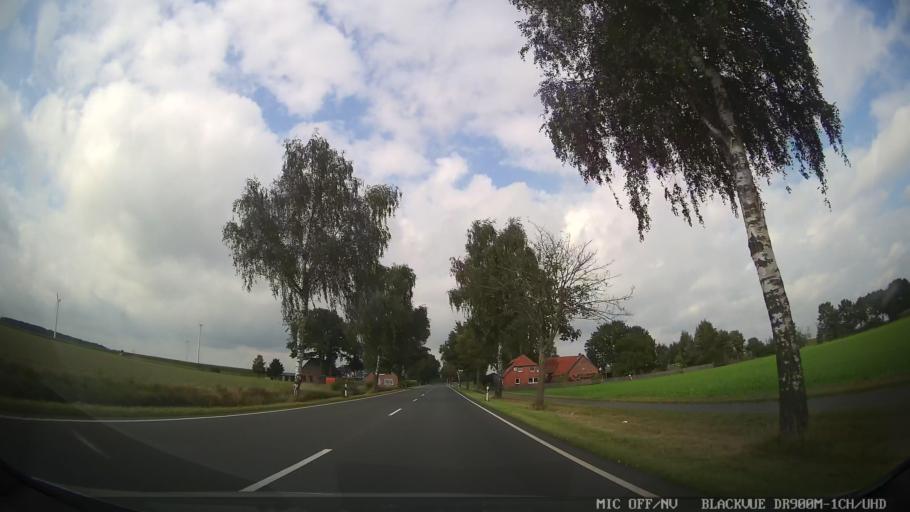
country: DE
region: Lower Saxony
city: Bergen
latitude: 52.7769
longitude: 9.9778
